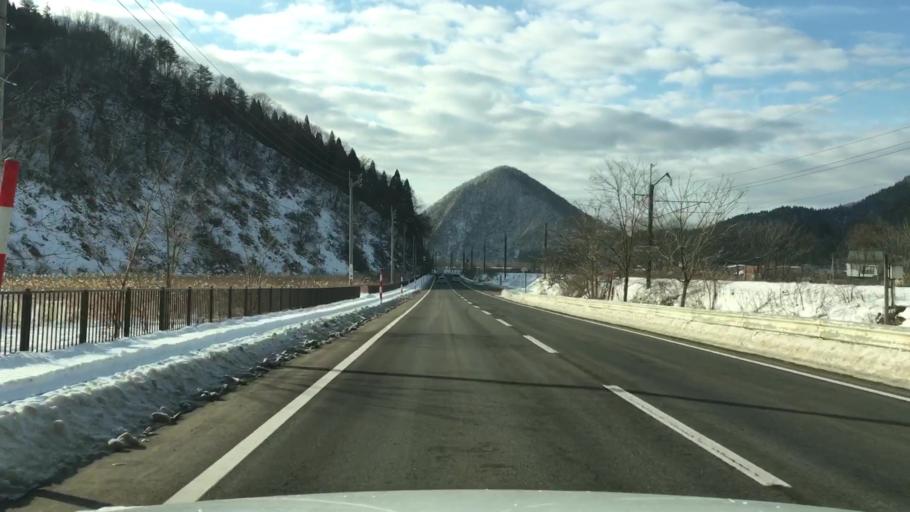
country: JP
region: Akita
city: Odate
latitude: 40.3694
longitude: 140.5993
